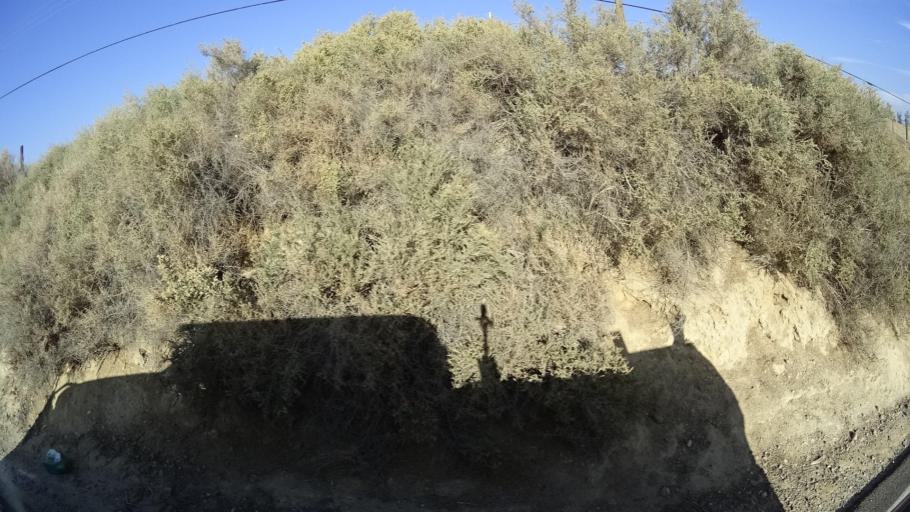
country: US
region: California
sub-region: Kern County
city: Oildale
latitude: 35.4390
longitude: -118.8940
